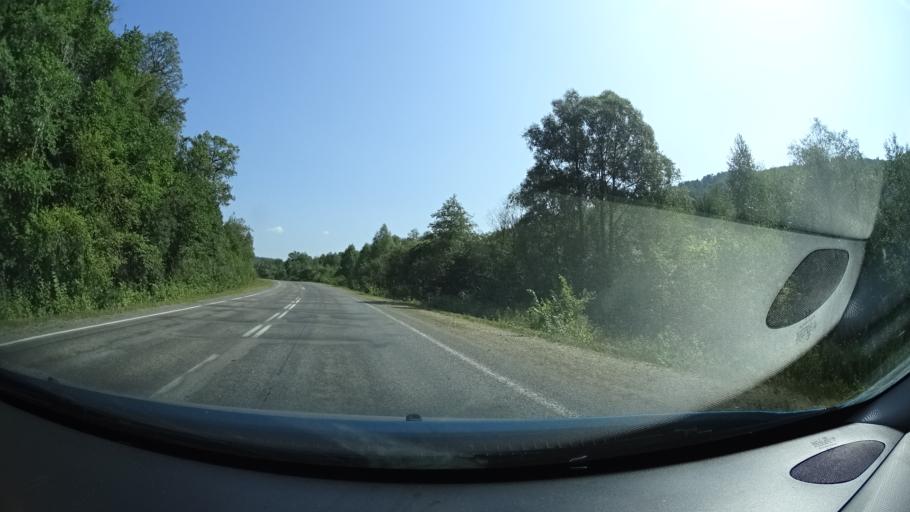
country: RU
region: Bashkortostan
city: Inzer
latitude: 54.3382
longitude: 57.0938
